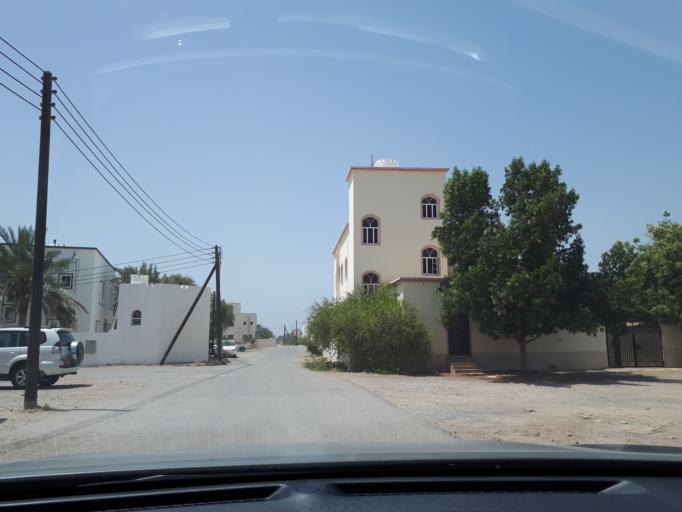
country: OM
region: Muhafazat Masqat
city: As Sib al Jadidah
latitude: 23.6881
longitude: 58.1123
